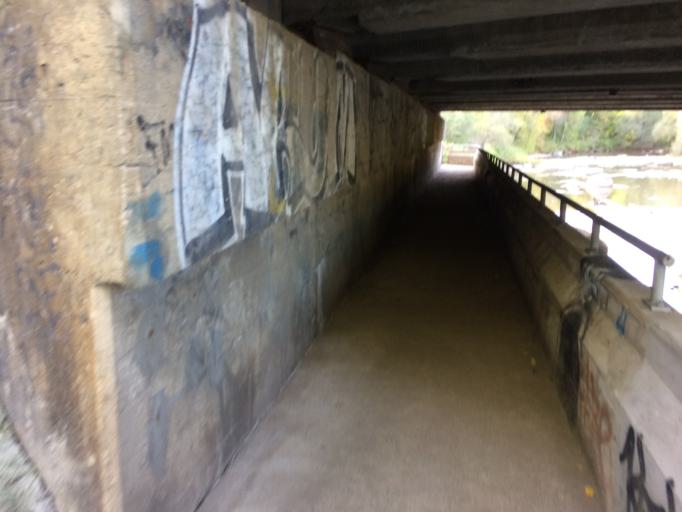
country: CA
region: Quebec
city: Quebec
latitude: 46.8079
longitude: -71.2685
